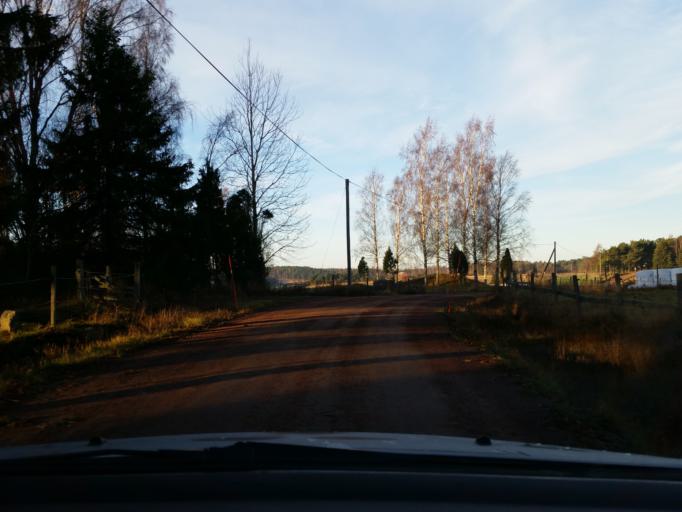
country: AX
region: Alands landsbygd
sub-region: Sund
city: Sund
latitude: 60.2712
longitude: 20.0902
